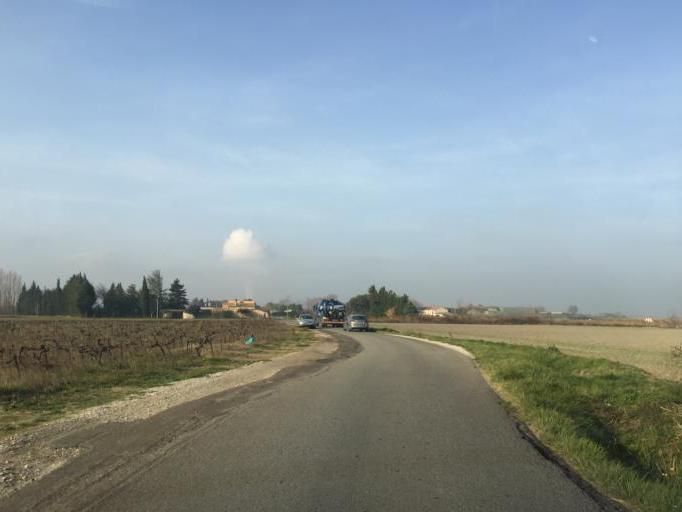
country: FR
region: Provence-Alpes-Cote d'Azur
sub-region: Departement du Vaucluse
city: Jonquieres
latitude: 44.1262
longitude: 4.8827
